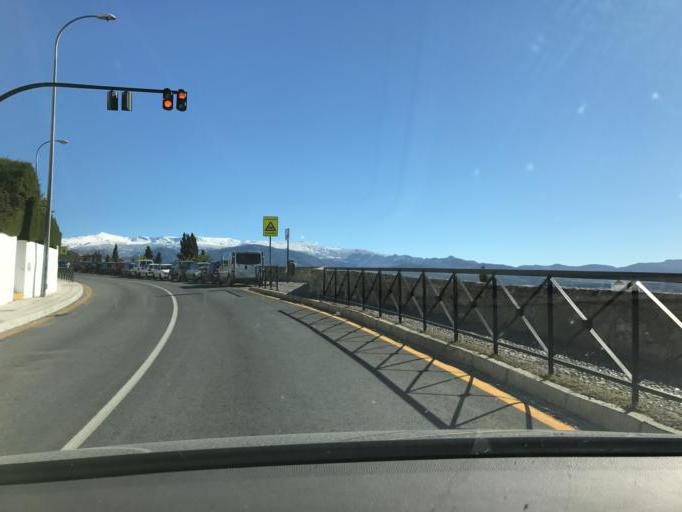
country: ES
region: Andalusia
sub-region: Provincia de Granada
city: Granada
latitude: 37.1836
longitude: -3.5972
